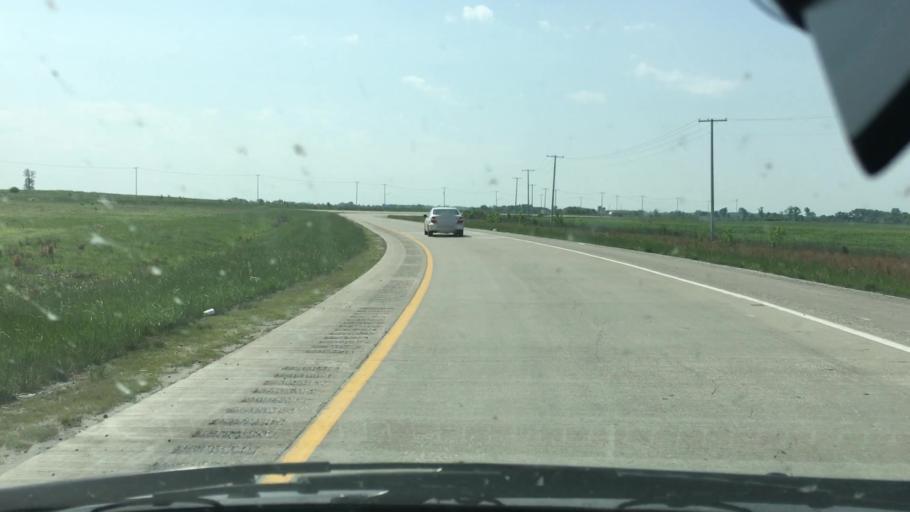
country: US
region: Indiana
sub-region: Daviess County
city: Washington
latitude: 38.6543
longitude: -87.1226
